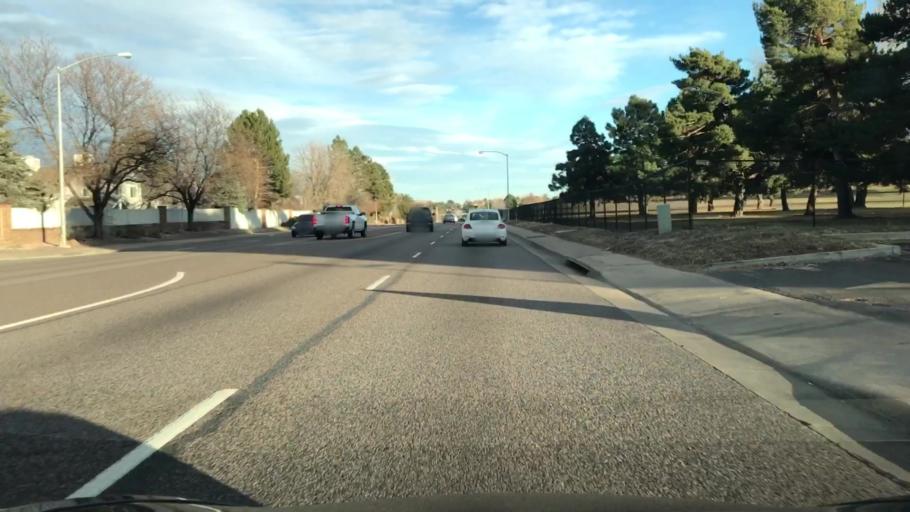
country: US
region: Colorado
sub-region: Adams County
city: Aurora
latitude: 39.6748
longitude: -104.8541
